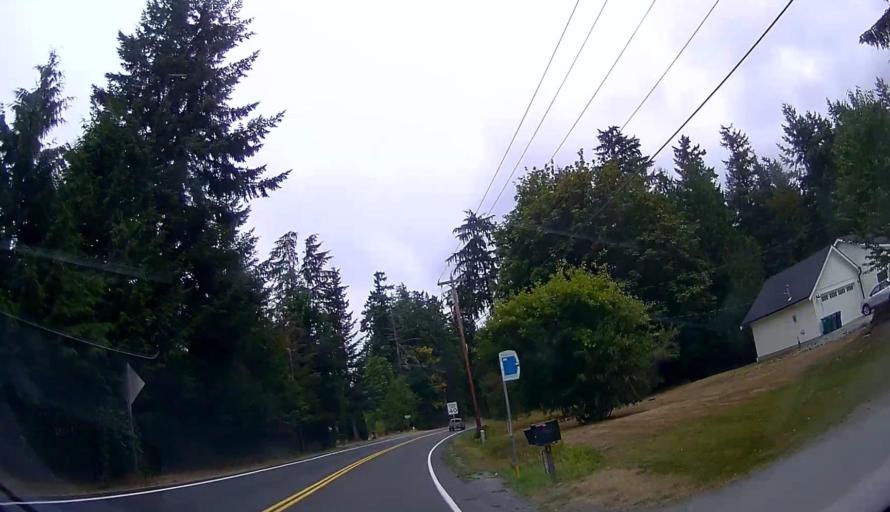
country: US
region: Washington
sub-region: Snohomish County
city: Warm Beach
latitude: 48.1683
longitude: -122.3575
